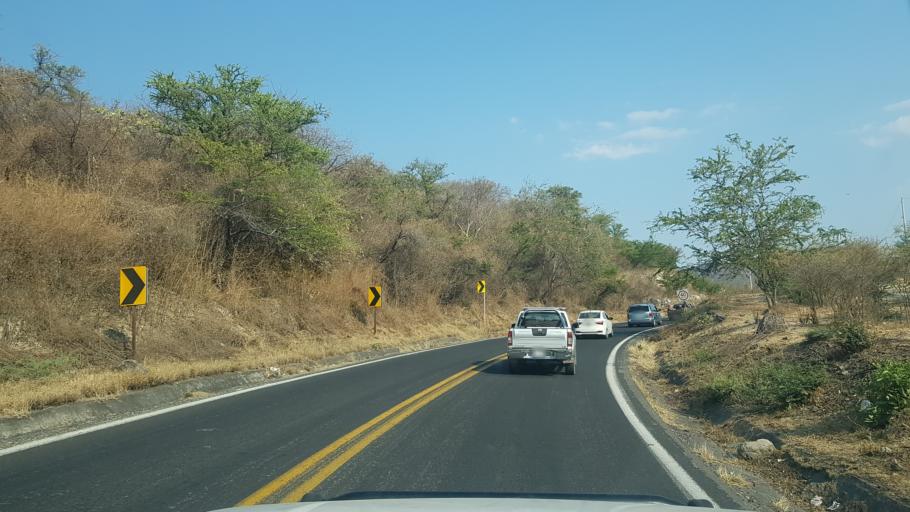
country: MX
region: Puebla
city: Calmeca
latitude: 18.6442
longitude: -98.6401
